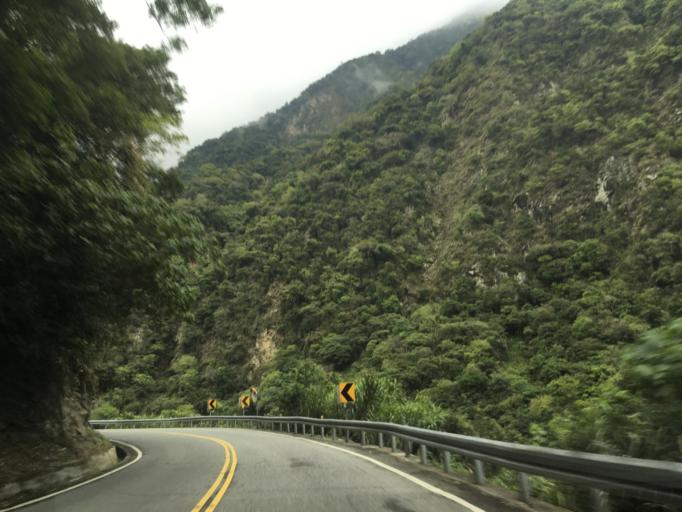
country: TW
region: Taiwan
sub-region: Hualien
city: Hualian
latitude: 24.1765
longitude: 121.5873
